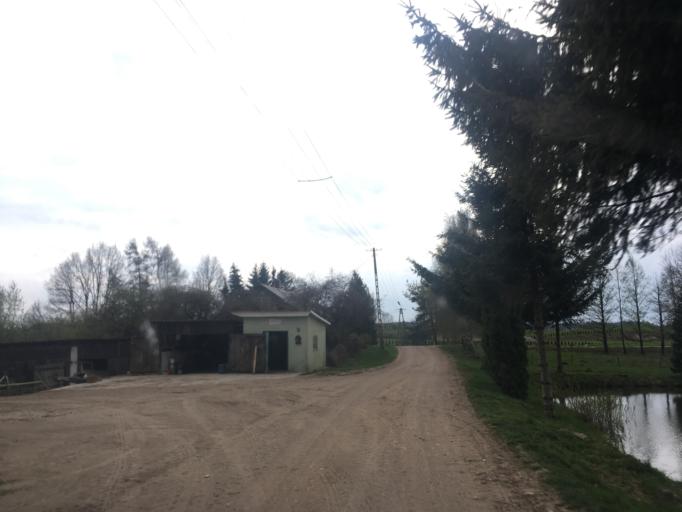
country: PL
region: Podlasie
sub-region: Powiat sejnenski
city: Punsk
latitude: 54.2848
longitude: 23.0930
